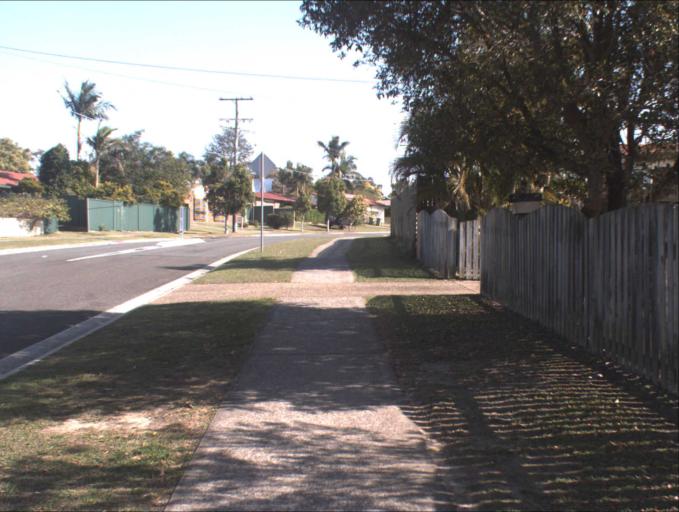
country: AU
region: Queensland
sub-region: Logan
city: Logan Reserve
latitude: -27.6877
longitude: 153.0933
